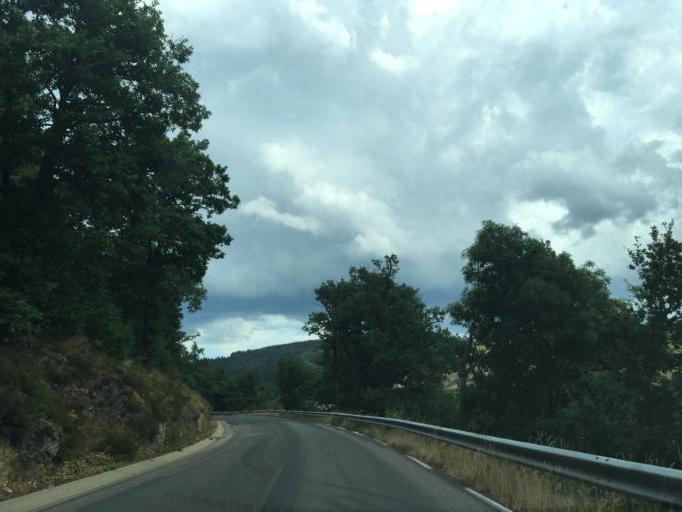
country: FR
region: Rhone-Alpes
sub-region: Departement de la Loire
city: Saint-Etienne
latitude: 45.4094
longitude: 4.4154
